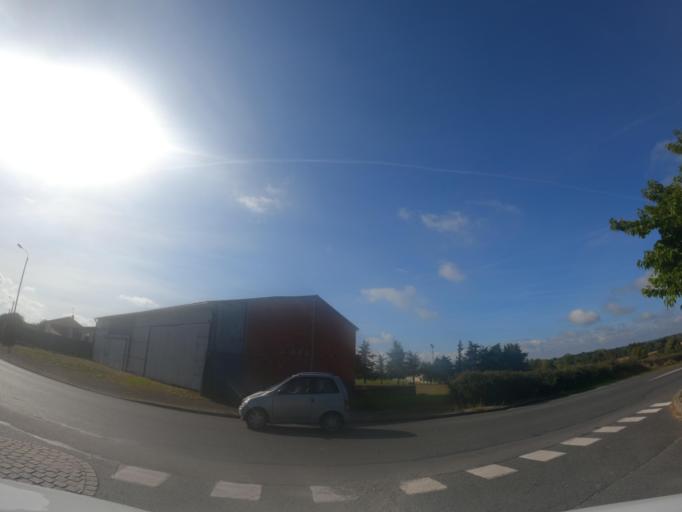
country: FR
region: Poitou-Charentes
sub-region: Departement des Deux-Sevres
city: Courlay
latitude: 46.7811
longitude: -0.5687
